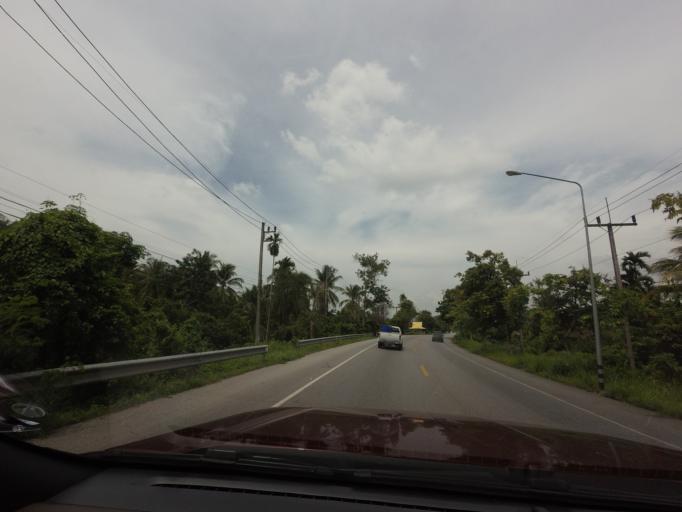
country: TH
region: Pattani
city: Mae Lan
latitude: 6.6221
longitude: 101.3055
